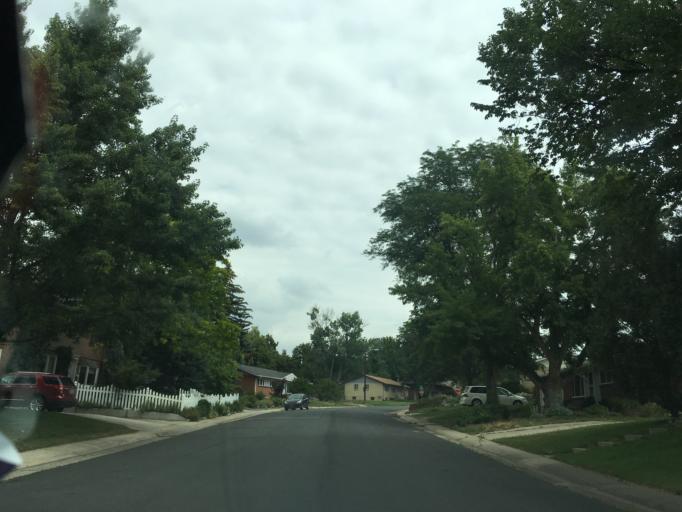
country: US
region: Colorado
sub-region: Arapahoe County
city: Sheridan
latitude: 39.6628
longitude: -105.0404
